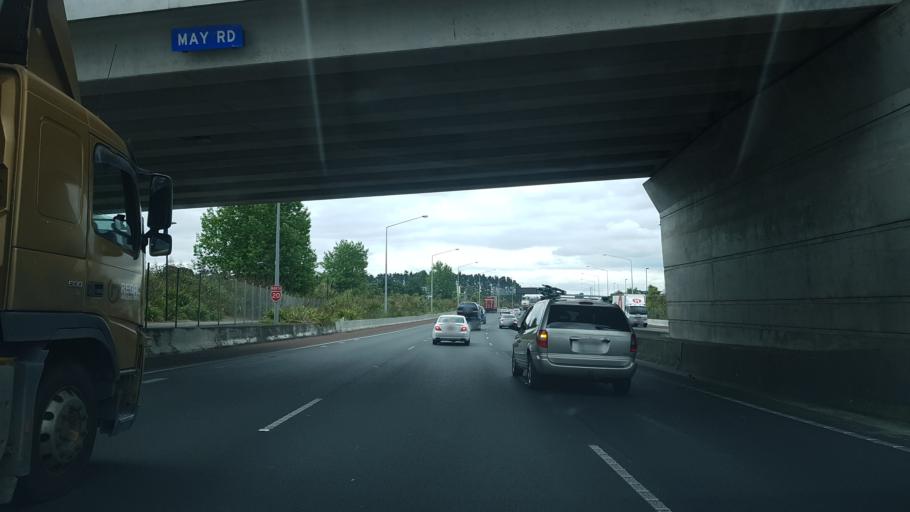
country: NZ
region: Auckland
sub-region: Auckland
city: Auckland
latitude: -36.9099
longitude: 174.7349
